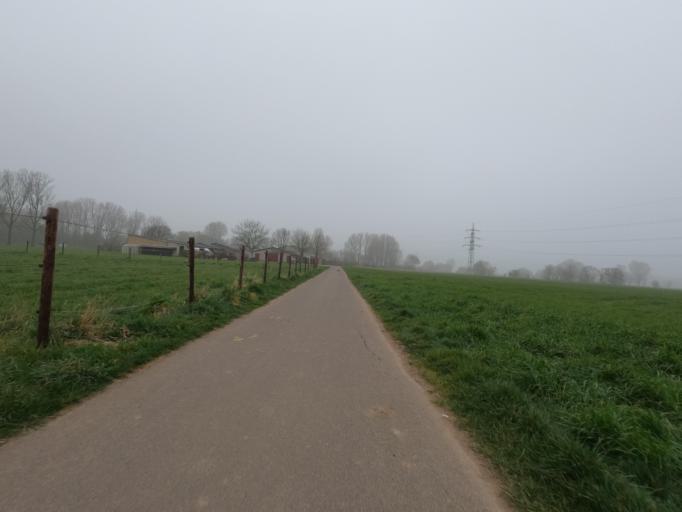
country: DE
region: North Rhine-Westphalia
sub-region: Regierungsbezirk Koln
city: Wassenberg
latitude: 51.0658
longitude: 6.1538
